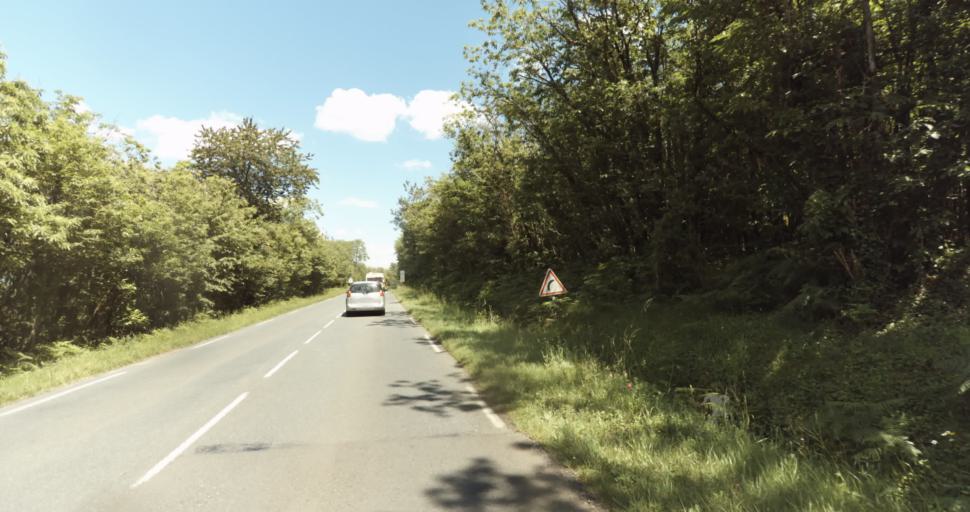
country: FR
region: Aquitaine
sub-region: Departement de la Dordogne
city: Le Bugue
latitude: 44.8425
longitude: 0.8724
